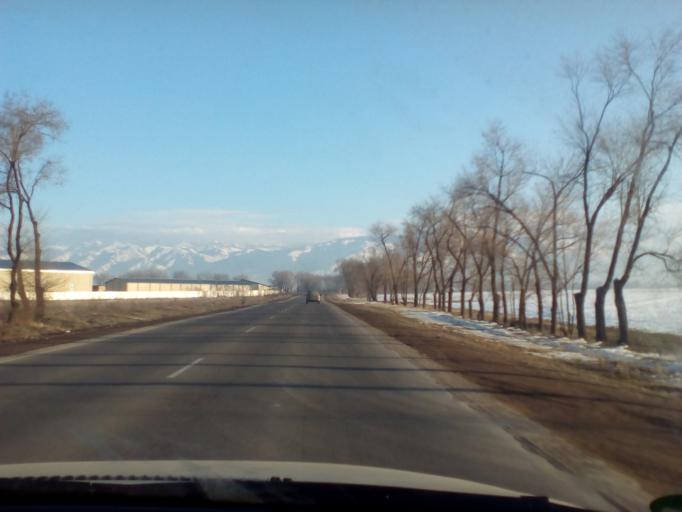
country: KZ
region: Almaty Oblysy
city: Burunday
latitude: 43.2173
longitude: 76.4119
